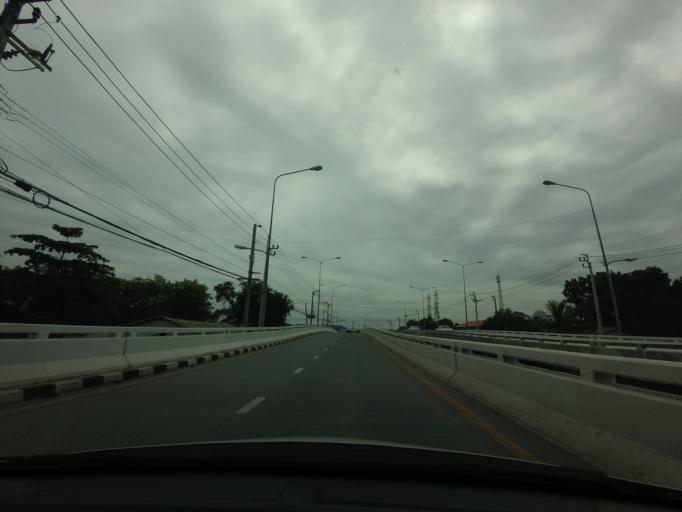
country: TH
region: Pathum Thani
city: Lam Luk Ka
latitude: 13.9118
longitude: 100.7703
